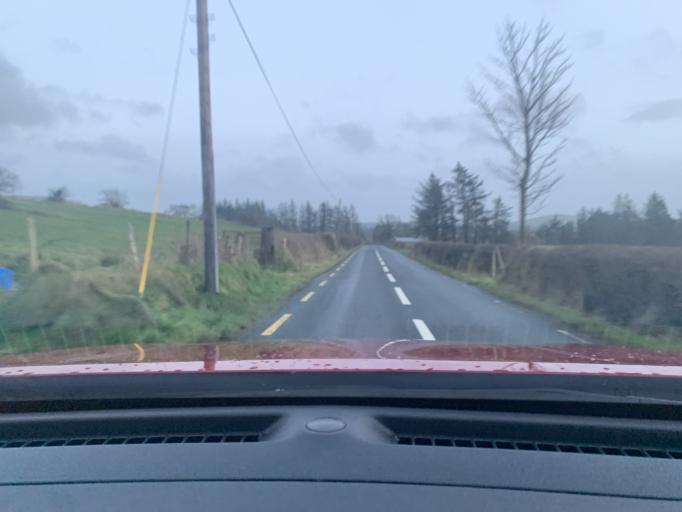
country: IE
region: Connaught
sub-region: Sligo
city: Ballymote
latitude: 54.0330
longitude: -8.4171
